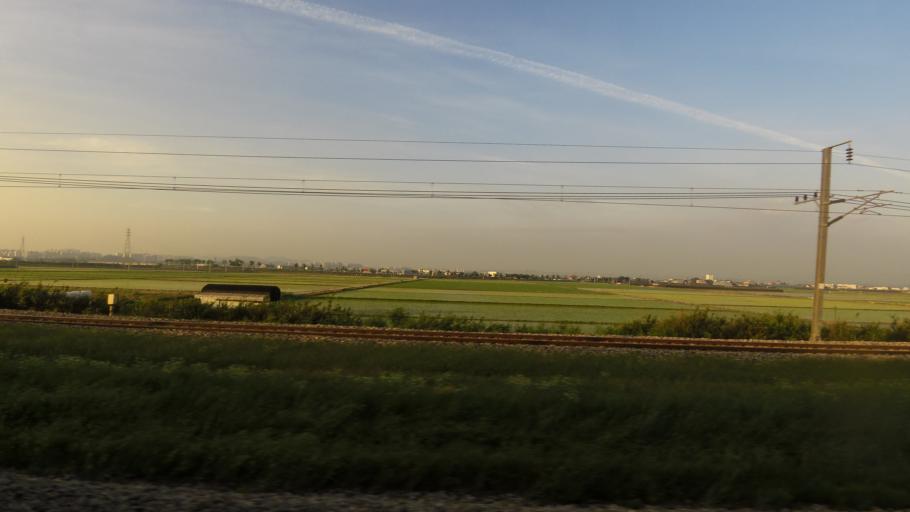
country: KR
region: Chungcheongnam-do
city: Seonghwan
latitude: 36.9615
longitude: 127.1133
